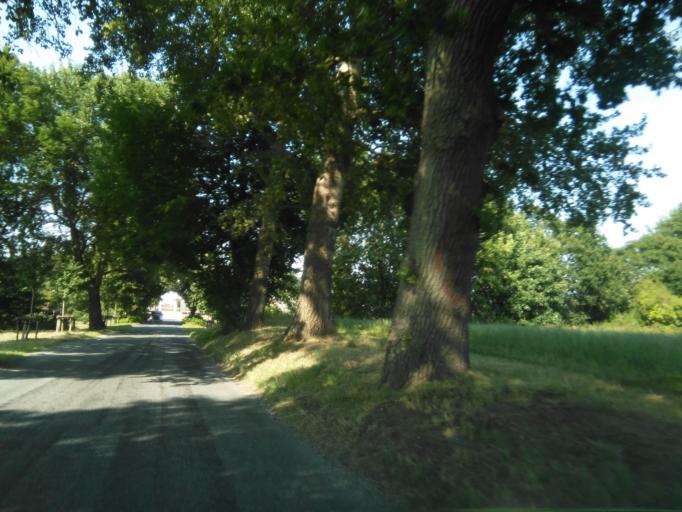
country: DK
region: Central Jutland
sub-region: Arhus Kommune
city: Kolt
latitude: 56.1369
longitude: 10.0774
